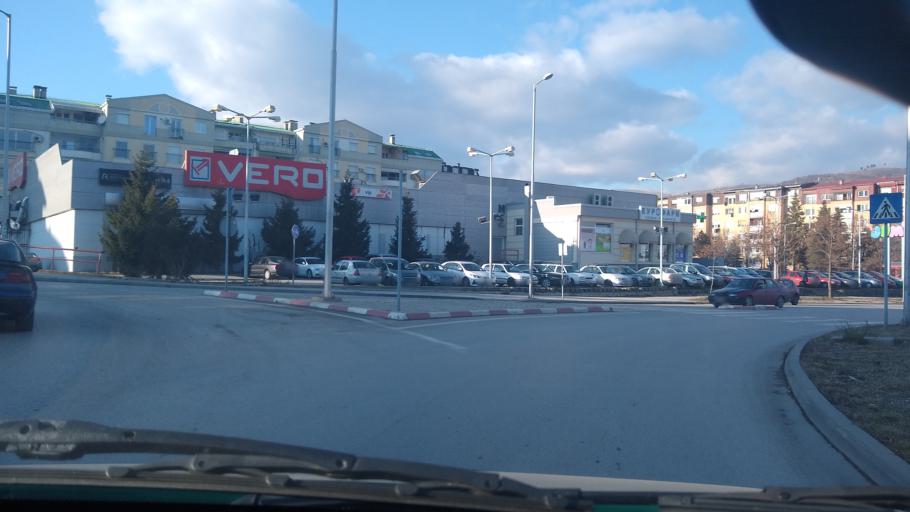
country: MK
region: Bitola
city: Bitola
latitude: 41.0260
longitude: 21.3133
